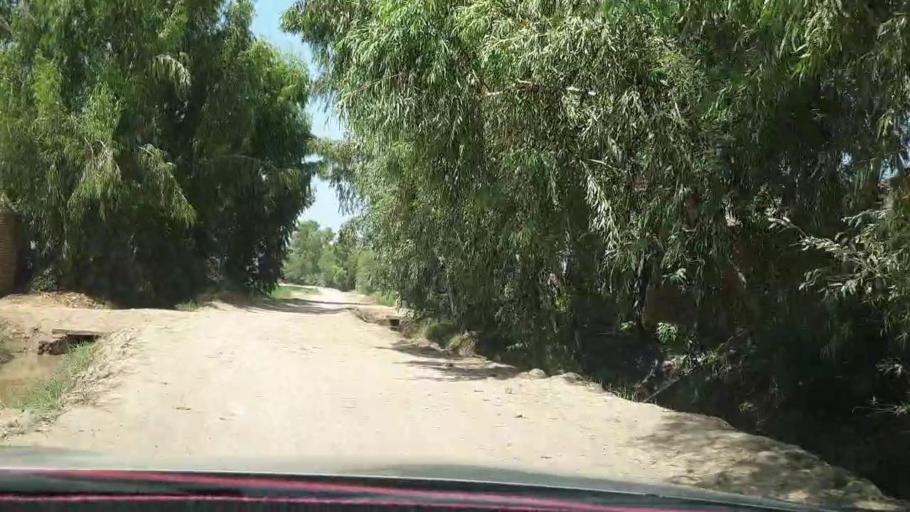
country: PK
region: Sindh
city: Warah
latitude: 27.5265
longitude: 67.8119
